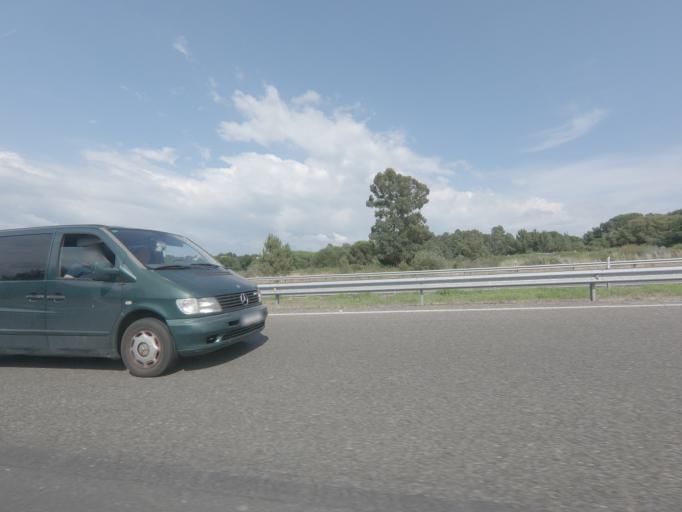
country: ES
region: Galicia
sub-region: Provincia de Ourense
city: Ourense
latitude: 42.3023
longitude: -7.8755
